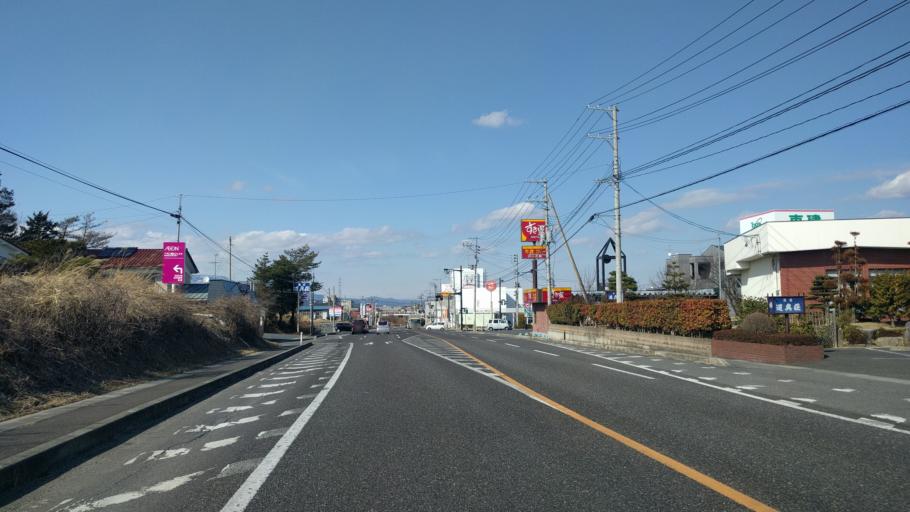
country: JP
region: Fukushima
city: Koriyama
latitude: 37.4401
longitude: 140.3798
